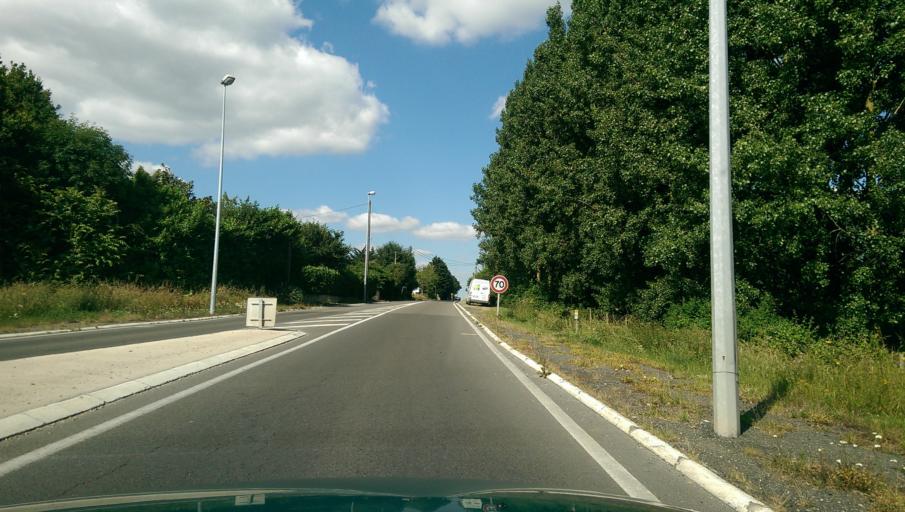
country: FR
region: Pays de la Loire
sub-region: Departement de la Loire-Atlantique
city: Lege
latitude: 46.8925
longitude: -1.5843
